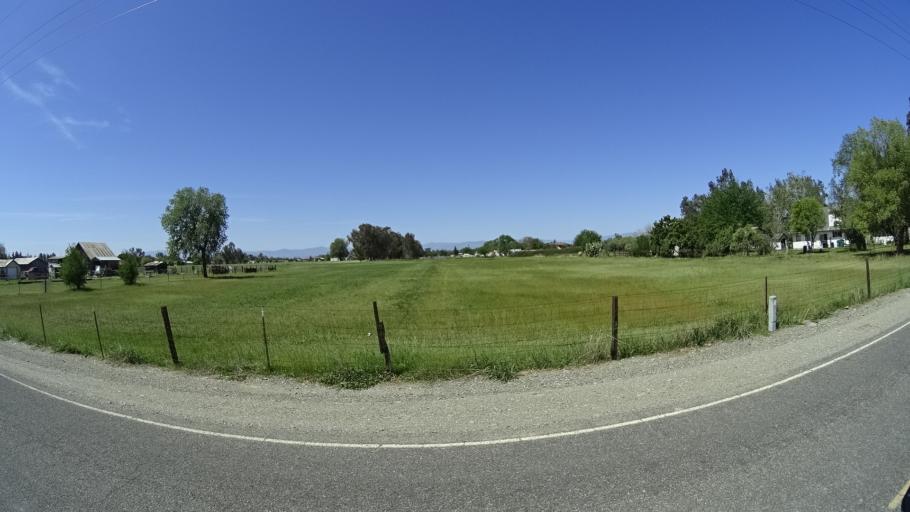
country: US
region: California
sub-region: Glenn County
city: Orland
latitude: 39.7292
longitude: -122.1780
